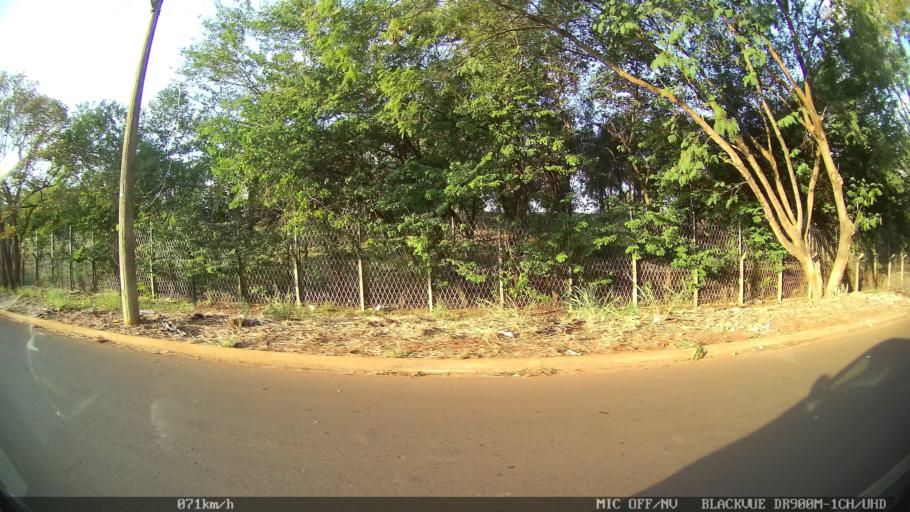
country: BR
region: Sao Paulo
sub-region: Ribeirao Preto
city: Ribeirao Preto
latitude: -21.1092
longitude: -47.8088
